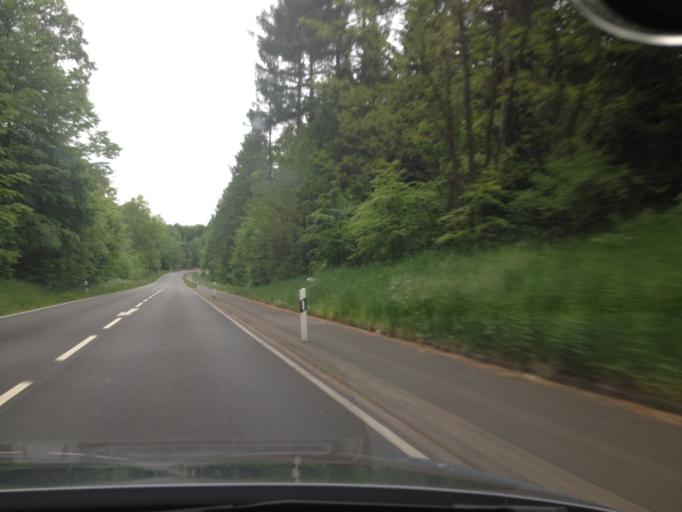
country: DE
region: Saarland
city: Kirkel
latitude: 49.2909
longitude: 7.2164
